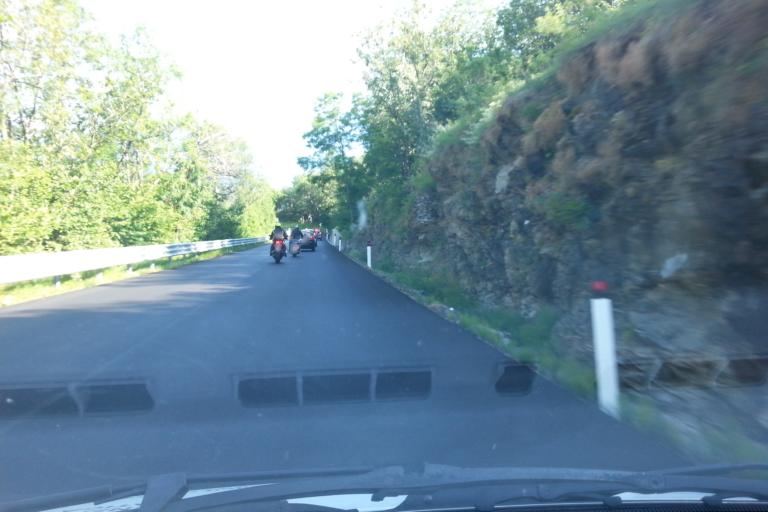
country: IT
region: Piedmont
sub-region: Provincia di Torino
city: Venaus
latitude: 45.1728
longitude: 7.0004
